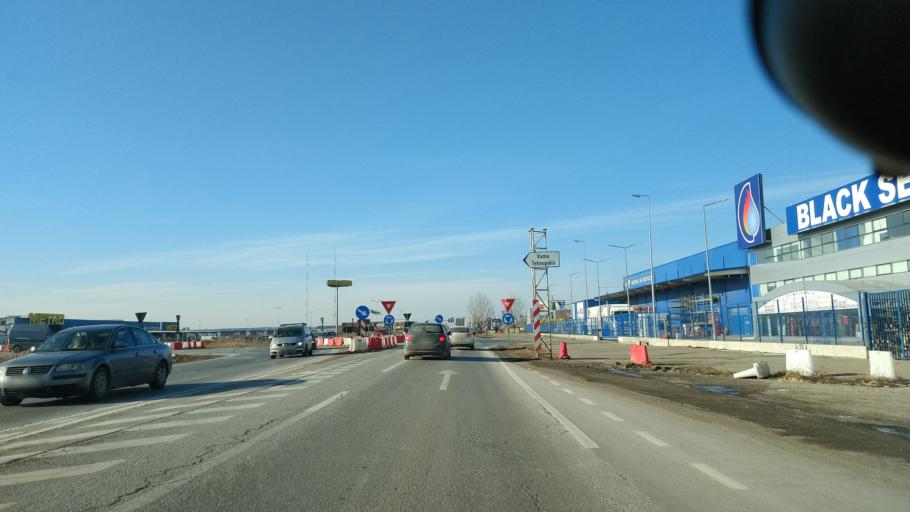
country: RO
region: Iasi
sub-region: Comuna Valea Lupului
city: Valea Lupului
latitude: 47.1809
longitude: 27.4734
